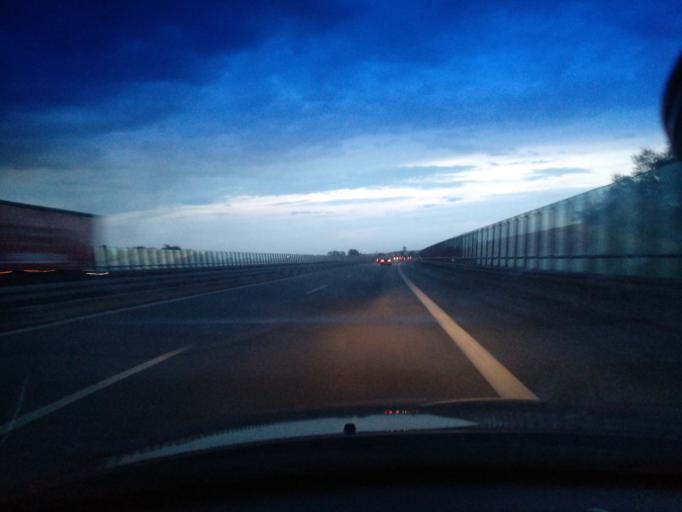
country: DE
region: Saxony
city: Kodersdorf
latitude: 51.2220
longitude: 14.8920
